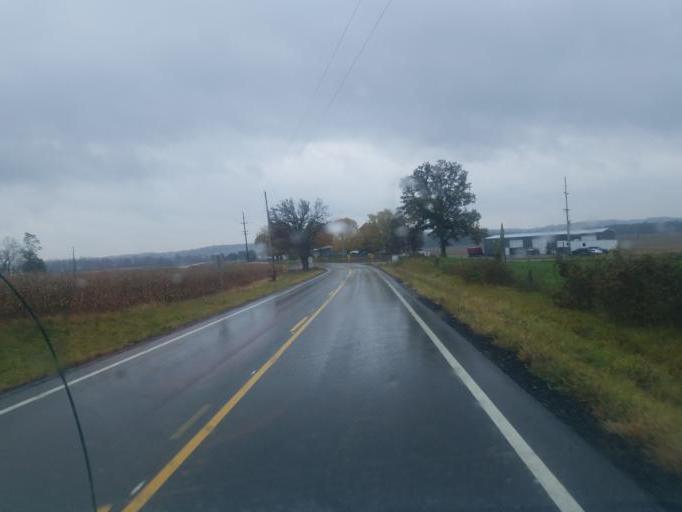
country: US
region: Ohio
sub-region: Knox County
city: Gambier
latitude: 40.3173
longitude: -82.4068
